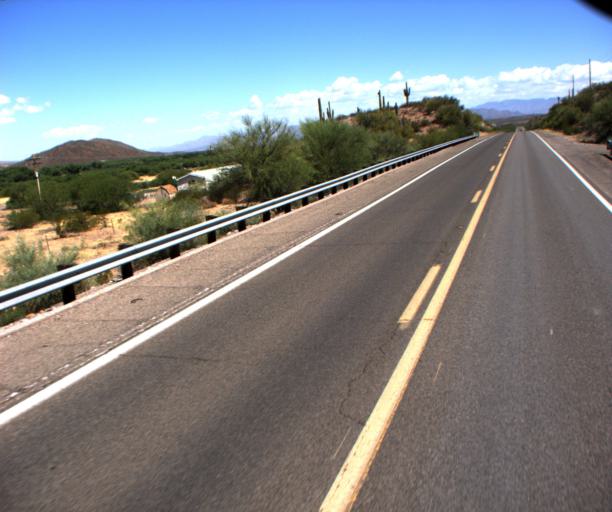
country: US
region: Arizona
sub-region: Pinal County
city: Mammoth
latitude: 32.8920
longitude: -110.7163
